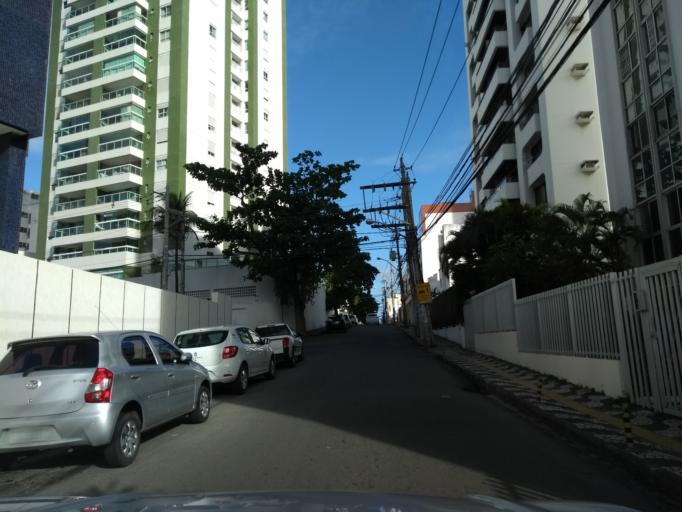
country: BR
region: Bahia
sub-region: Salvador
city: Salvador
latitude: -12.9972
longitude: -38.4542
